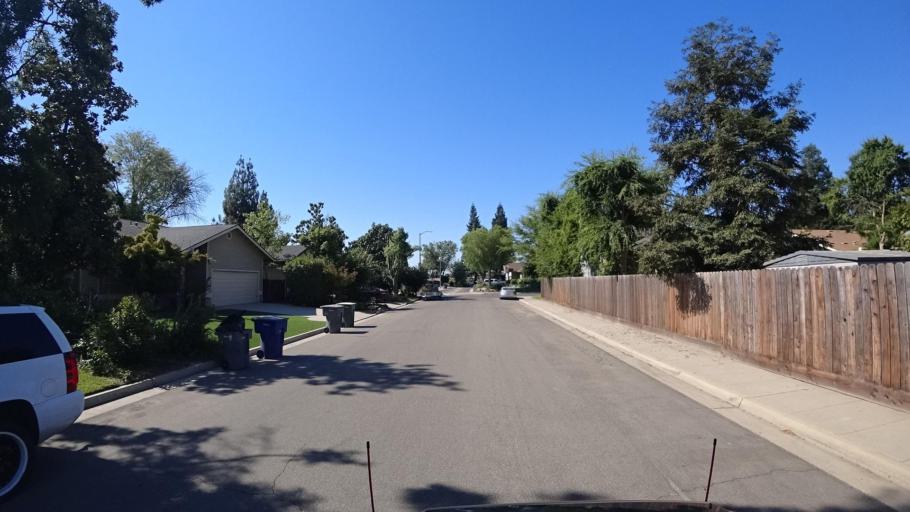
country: US
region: California
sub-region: Fresno County
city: Sunnyside
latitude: 36.7452
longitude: -119.6780
